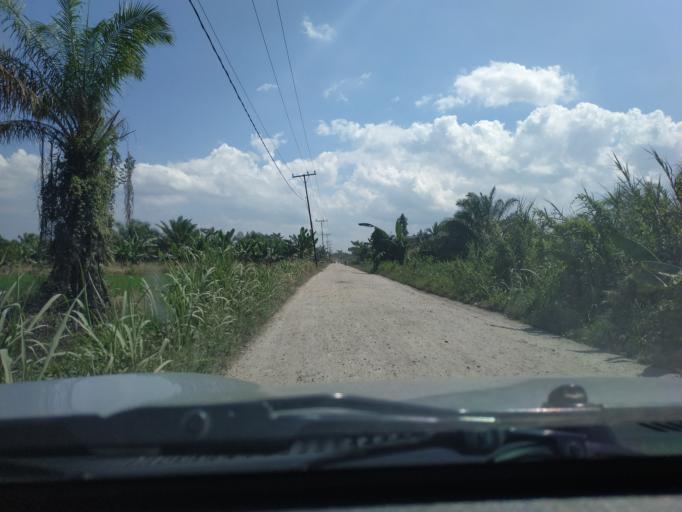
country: ID
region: North Sumatra
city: Tanjungbalai
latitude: 2.8834
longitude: 99.8616
